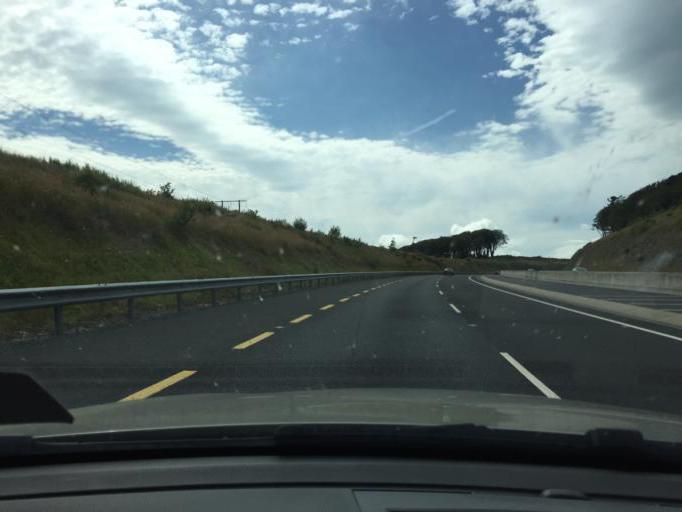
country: IE
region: Leinster
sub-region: Kilkenny
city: Mooncoin
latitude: 52.2345
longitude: -7.2245
